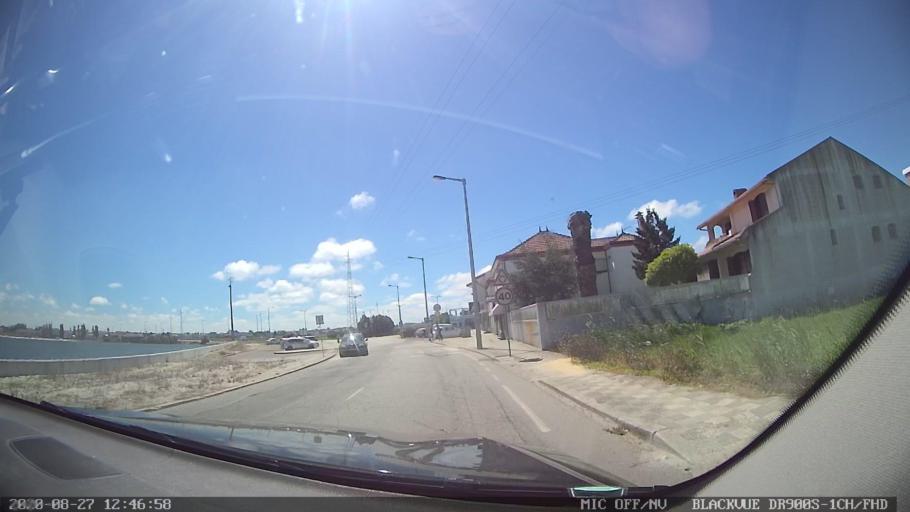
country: PT
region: Aveiro
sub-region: Ilhavo
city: Ilhavo
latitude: 40.6091
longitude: -8.6846
